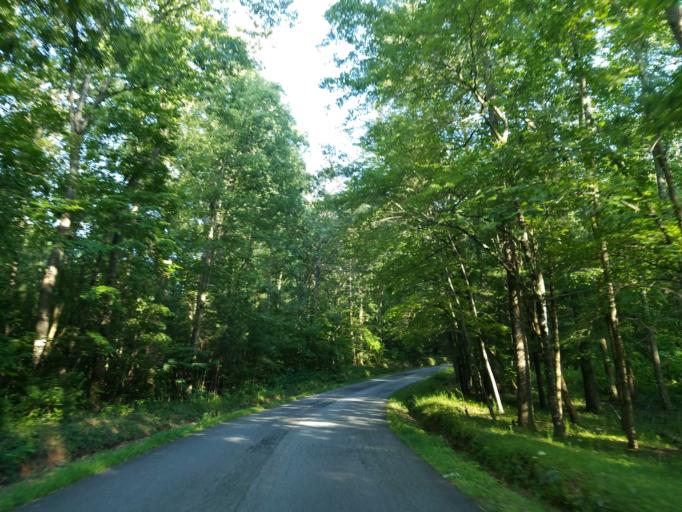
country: US
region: Georgia
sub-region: Gilmer County
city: Ellijay
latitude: 34.6408
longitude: -84.3323
